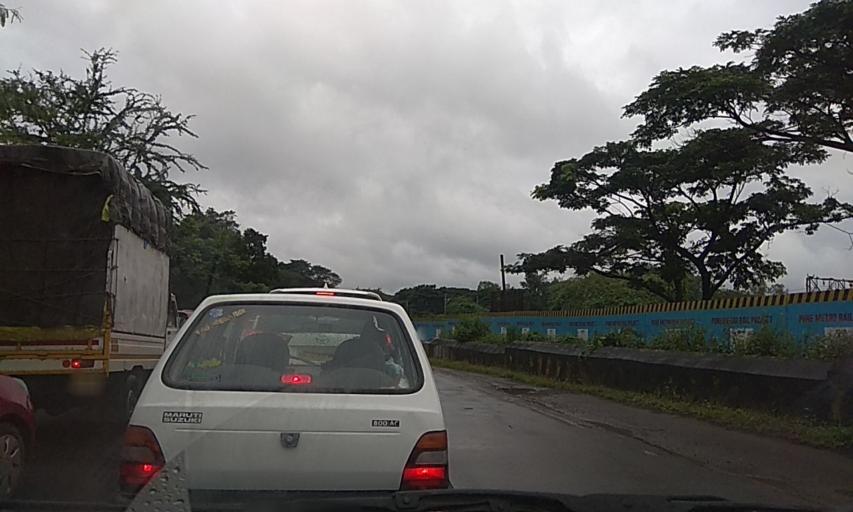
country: IN
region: Maharashtra
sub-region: Pune Division
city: Shivaji Nagar
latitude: 18.5452
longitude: 73.8471
